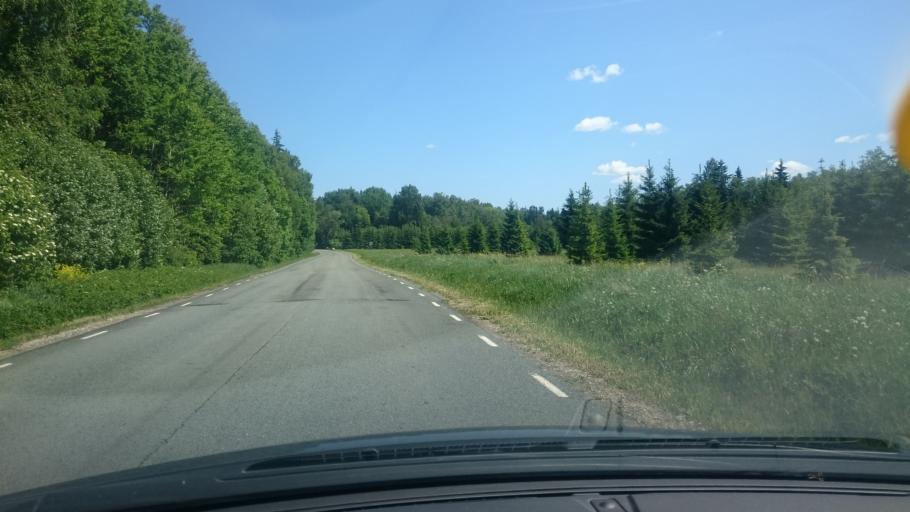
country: EE
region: Harju
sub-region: Rae vald
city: Vaida
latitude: 59.2030
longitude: 24.9138
